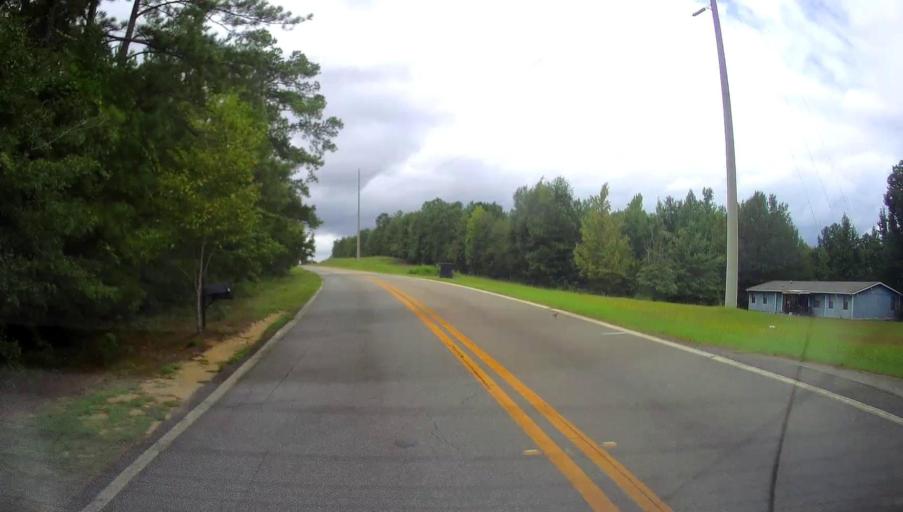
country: US
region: Georgia
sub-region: Bibb County
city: Macon
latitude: 32.7915
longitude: -83.5190
